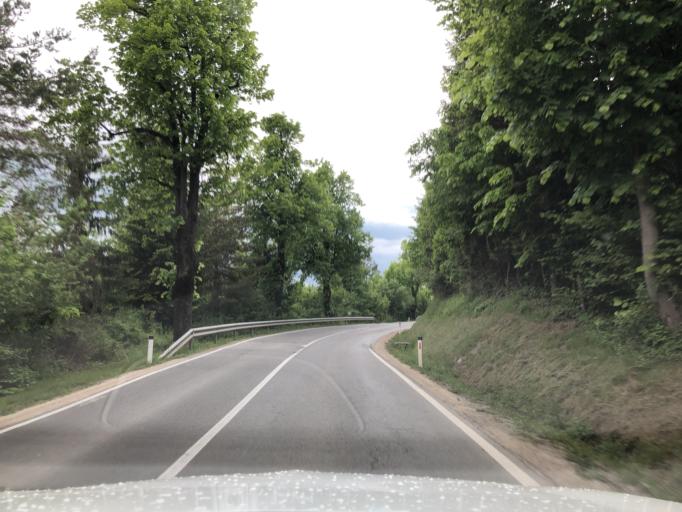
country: SI
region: Cerknica
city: Cerknica
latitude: 45.7975
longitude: 14.3356
